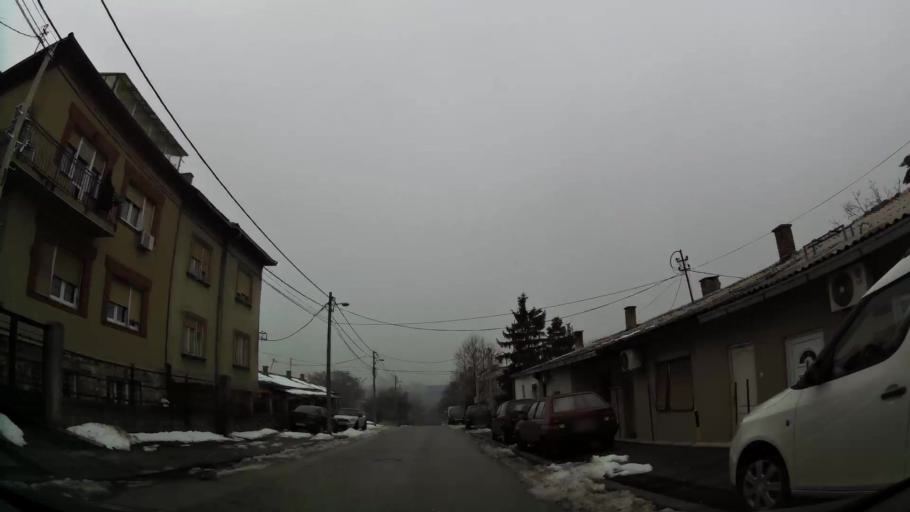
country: RS
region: Central Serbia
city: Belgrade
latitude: 44.7943
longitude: 20.4568
